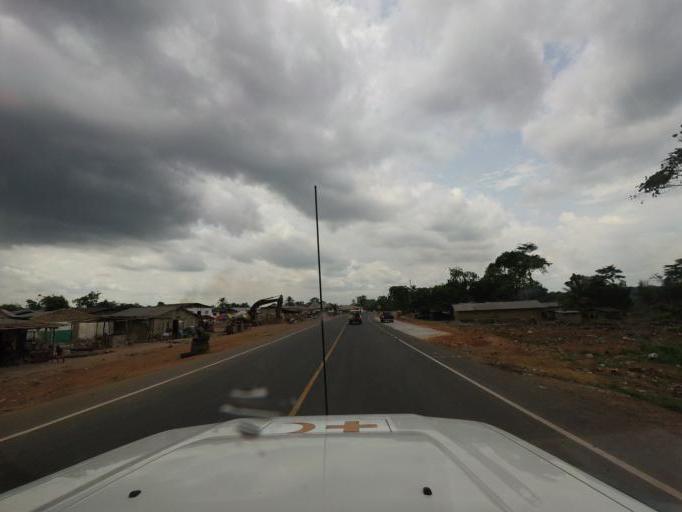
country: LR
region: Margibi
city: Kakata
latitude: 6.6868
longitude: -10.2105
